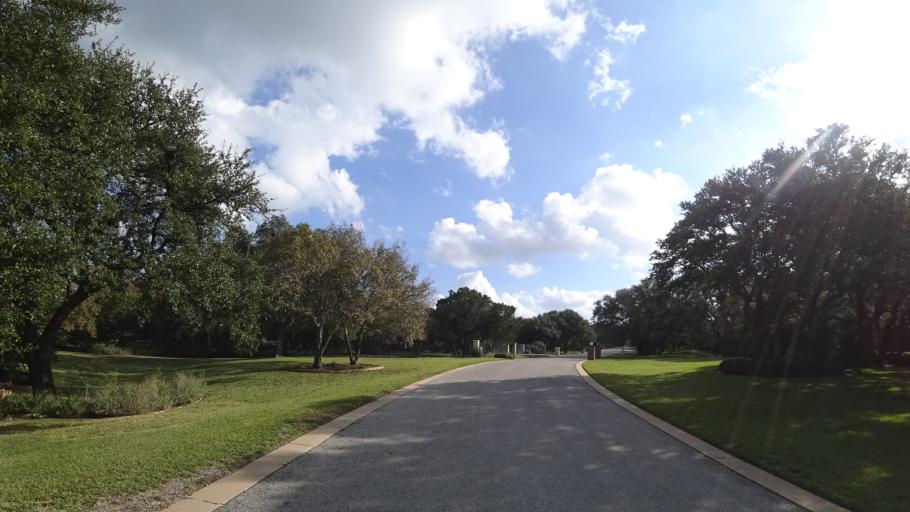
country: US
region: Texas
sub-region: Travis County
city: Barton Creek
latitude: 30.2852
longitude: -97.8815
